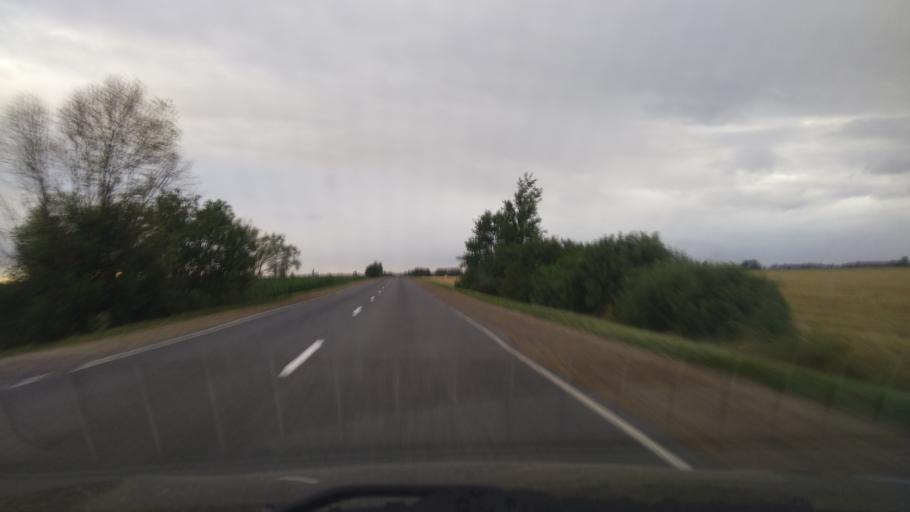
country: BY
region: Brest
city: Byaroza
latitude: 52.4400
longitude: 24.9768
